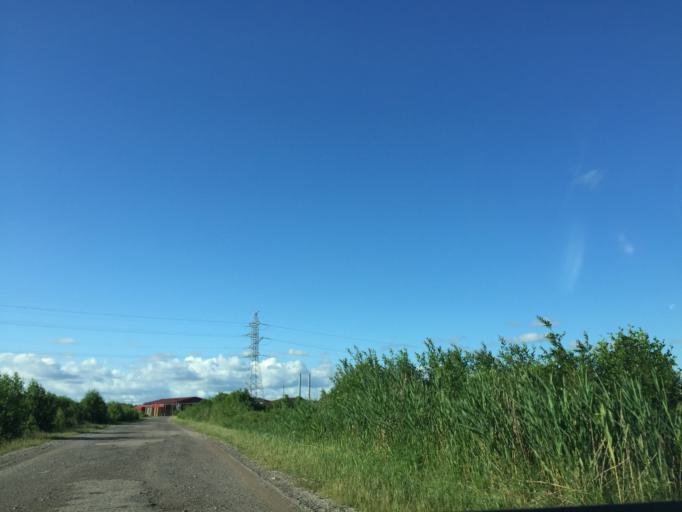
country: LV
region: Ventspils
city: Ventspils
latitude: 57.4001
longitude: 21.6491
